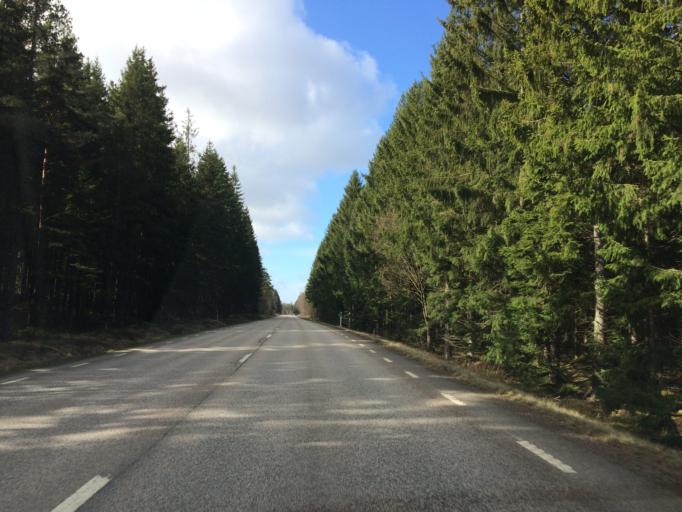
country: SE
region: Halland
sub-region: Laholms Kommun
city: Knared
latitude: 56.4916
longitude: 13.4020
